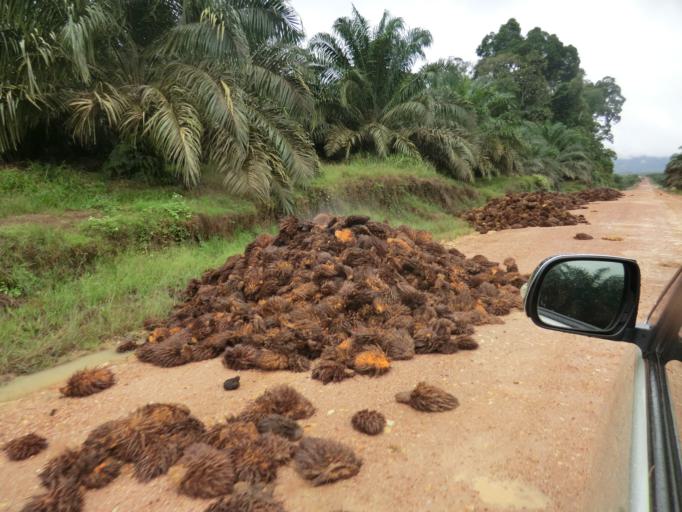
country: MY
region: Sarawak
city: Simanggang
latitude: 0.9611
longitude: 111.8863
